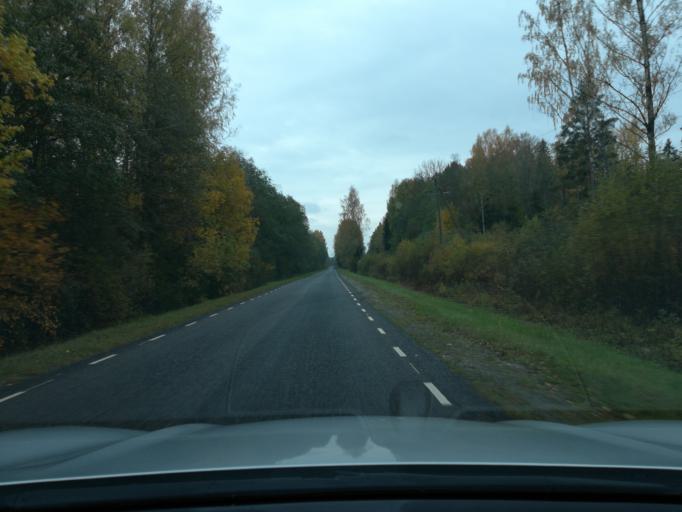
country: EE
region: Ida-Virumaa
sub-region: Johvi vald
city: Johvi
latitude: 59.0432
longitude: 27.3955
